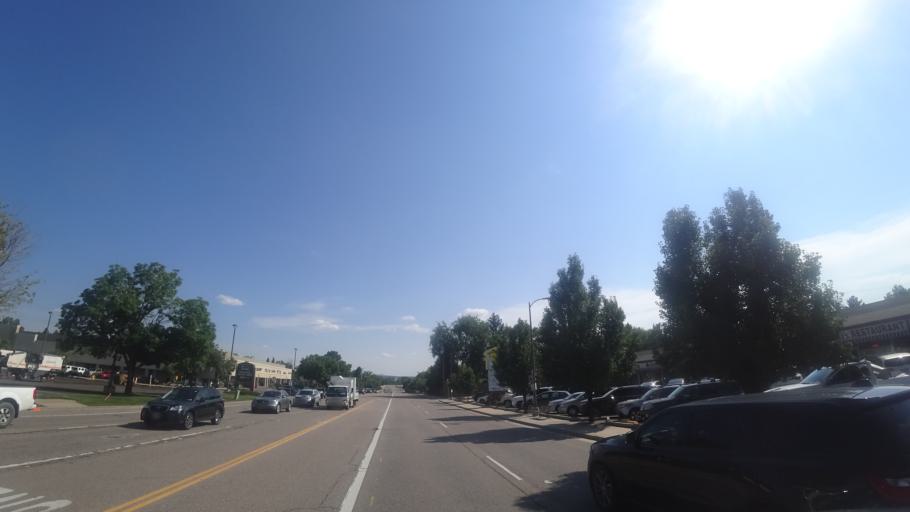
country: US
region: Colorado
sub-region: Arapahoe County
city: Greenwood Village
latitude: 39.6092
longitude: -104.9601
